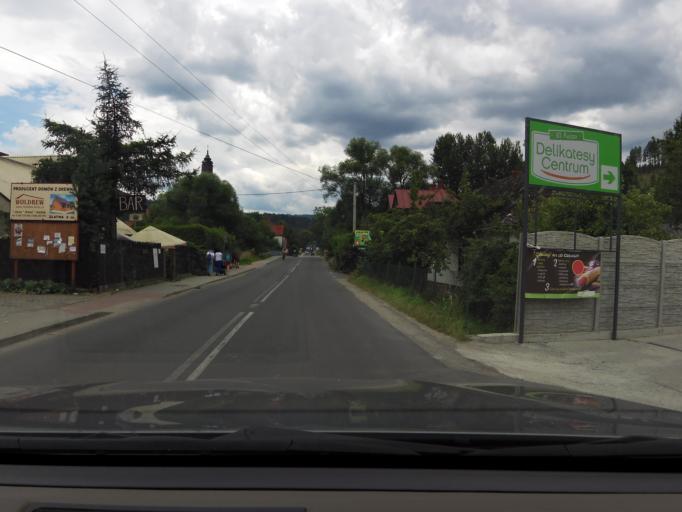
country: PL
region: Silesian Voivodeship
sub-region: Powiat zywiecki
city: Ujsoly
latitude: 49.4806
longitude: 19.1406
